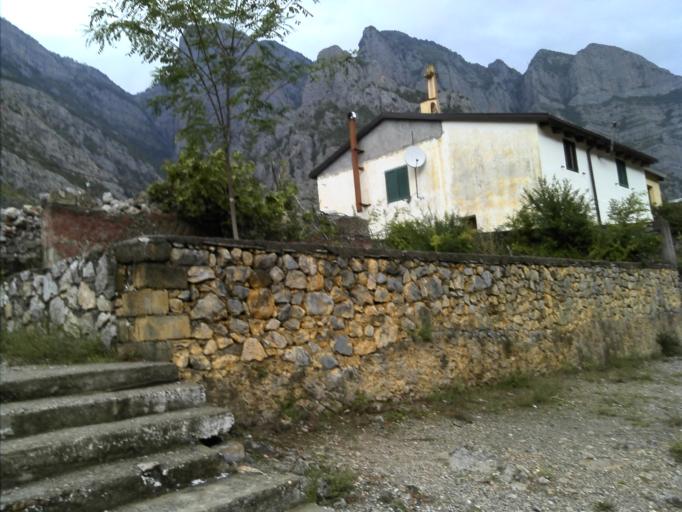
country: AL
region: Shkoder
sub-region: Rrethi i Malesia e Madhe
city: Kastrat
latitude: 42.4637
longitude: 19.5623
